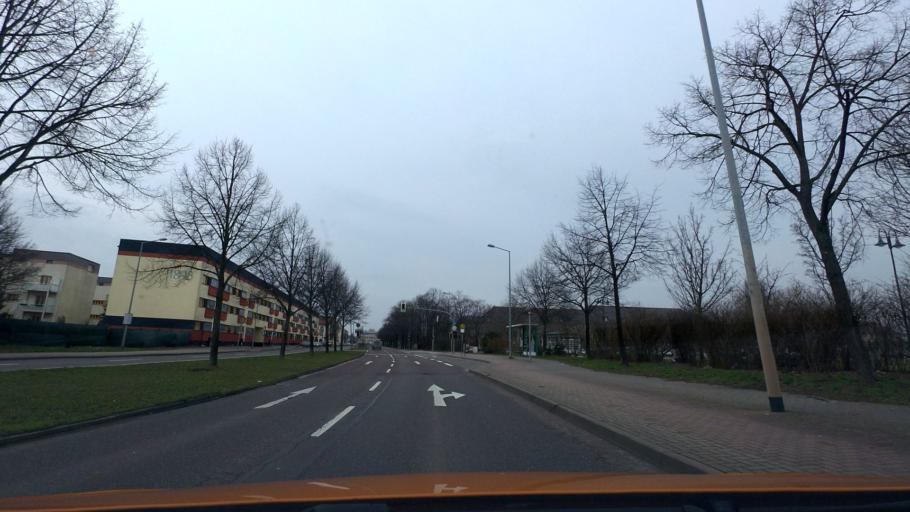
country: DE
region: Saxony-Anhalt
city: Neue Neustadt
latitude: 52.1322
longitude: 11.6737
